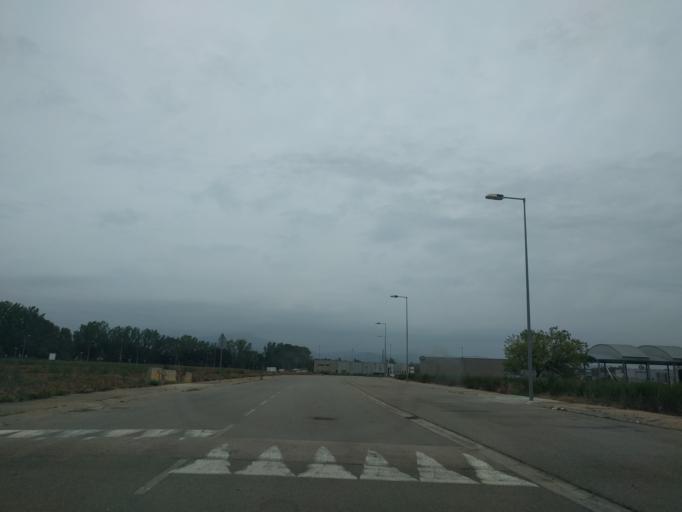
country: ES
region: Catalonia
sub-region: Provincia de Girona
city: Vilablareix
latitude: 41.9649
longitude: 2.7726
